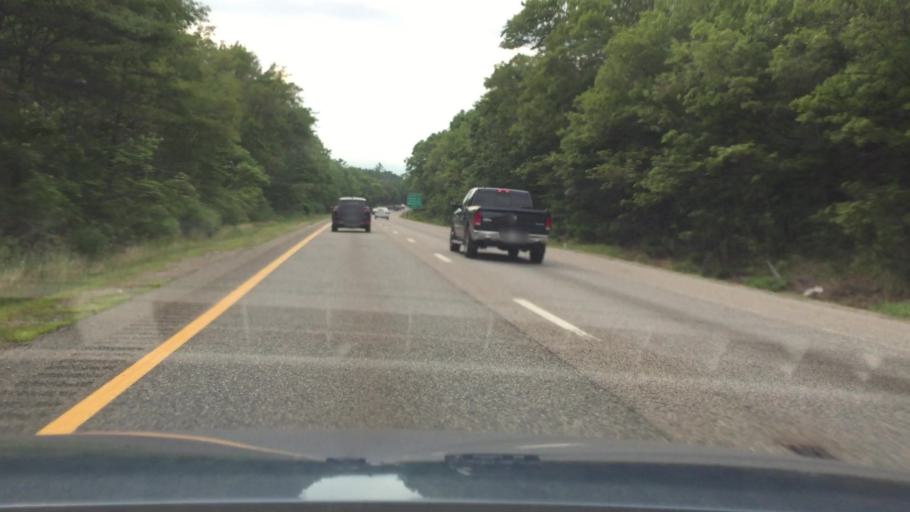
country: US
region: Massachusetts
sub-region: Plymouth County
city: Rockland
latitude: 42.1687
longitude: -70.9002
